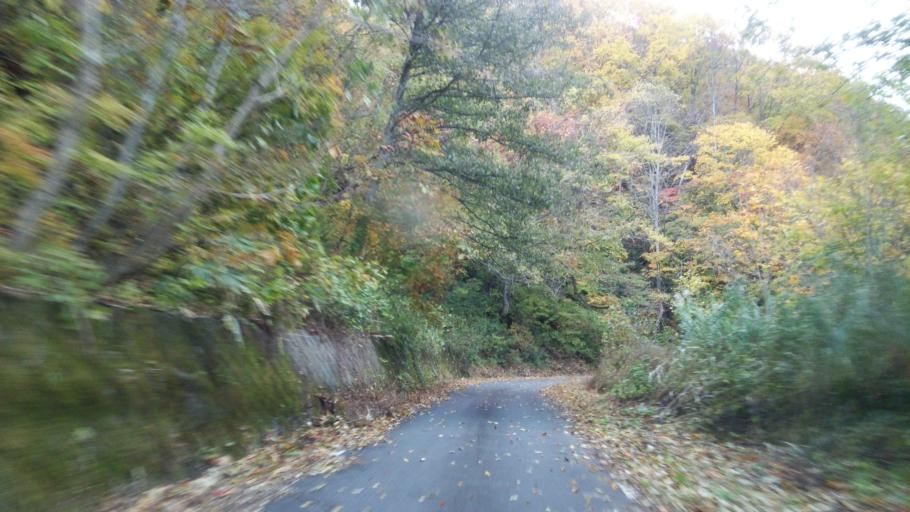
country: JP
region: Fukushima
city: Kitakata
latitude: 37.3856
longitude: 139.7266
